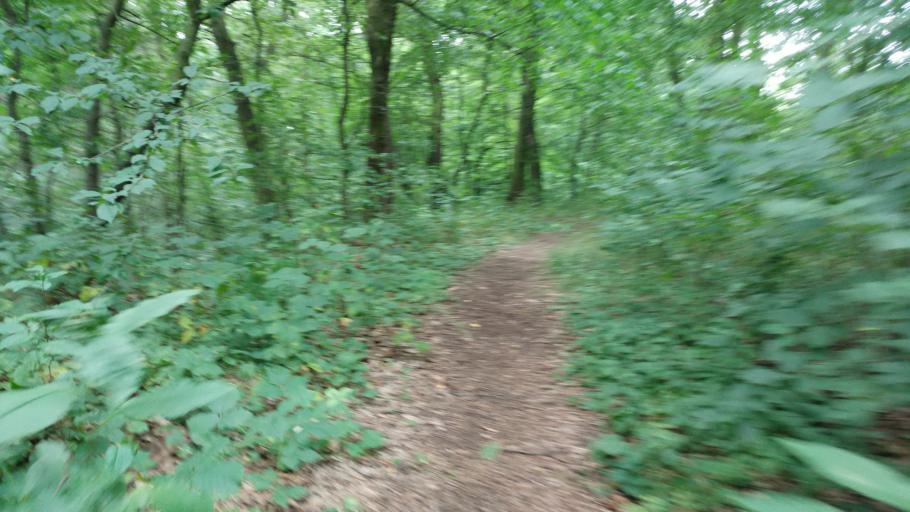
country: CZ
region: Central Bohemia
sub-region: Okres Praha-Zapad
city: Pruhonice
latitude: 50.0354
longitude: 14.5440
